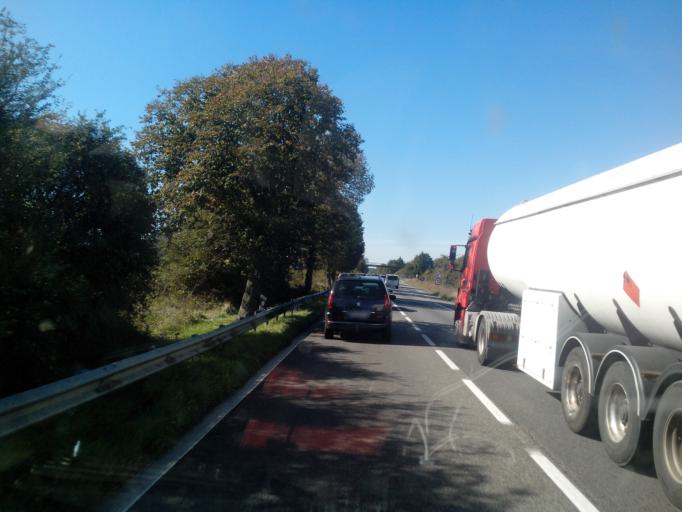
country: FR
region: Pays de la Loire
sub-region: Departement de la Loire-Atlantique
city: Malville
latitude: 47.3462
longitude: -1.8627
